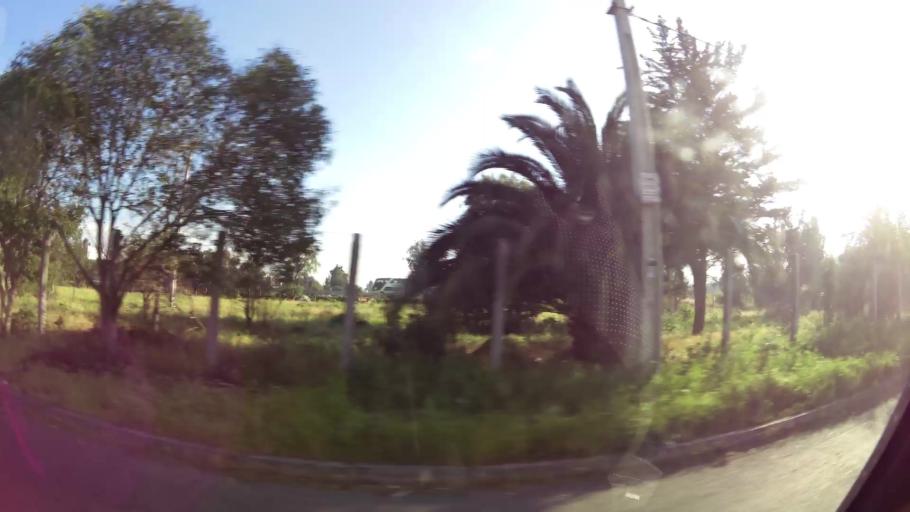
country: CL
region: Santiago Metropolitan
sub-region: Provincia de Santiago
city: Lo Prado
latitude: -33.4496
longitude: -70.7632
